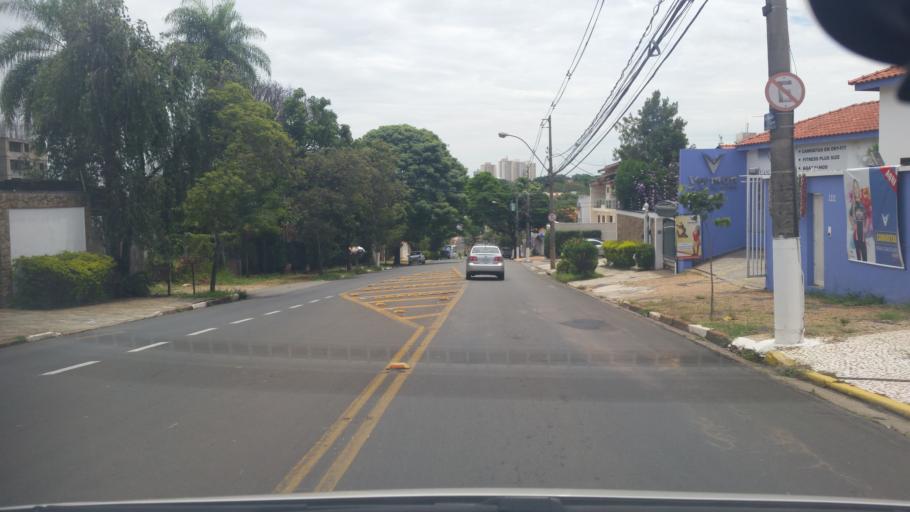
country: BR
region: Sao Paulo
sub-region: Campinas
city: Campinas
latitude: -22.8700
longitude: -47.0594
